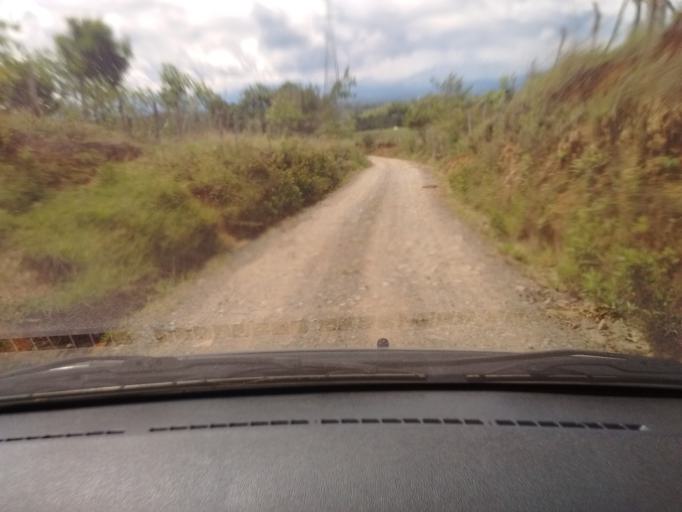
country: CO
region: Cauca
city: El Tambo
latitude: 2.4554
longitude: -76.8232
